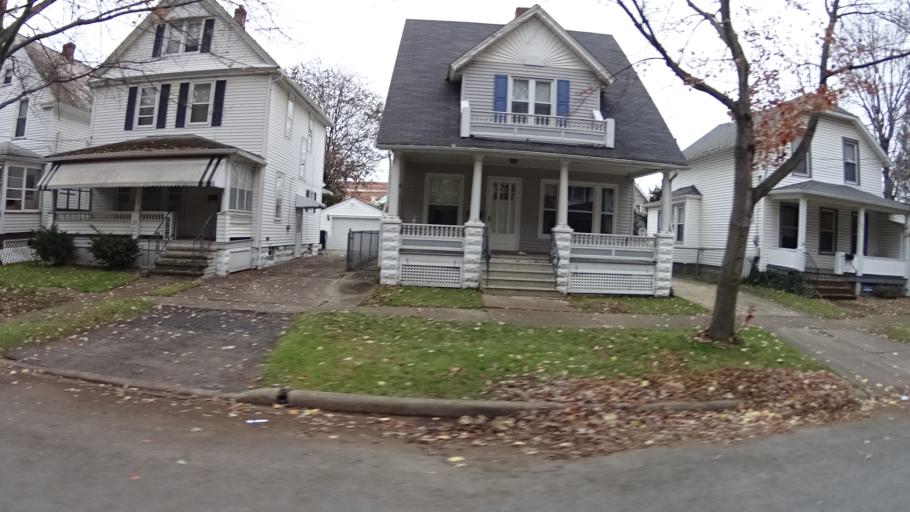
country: US
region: Ohio
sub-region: Lorain County
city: Elyria
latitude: 41.3598
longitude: -82.1091
